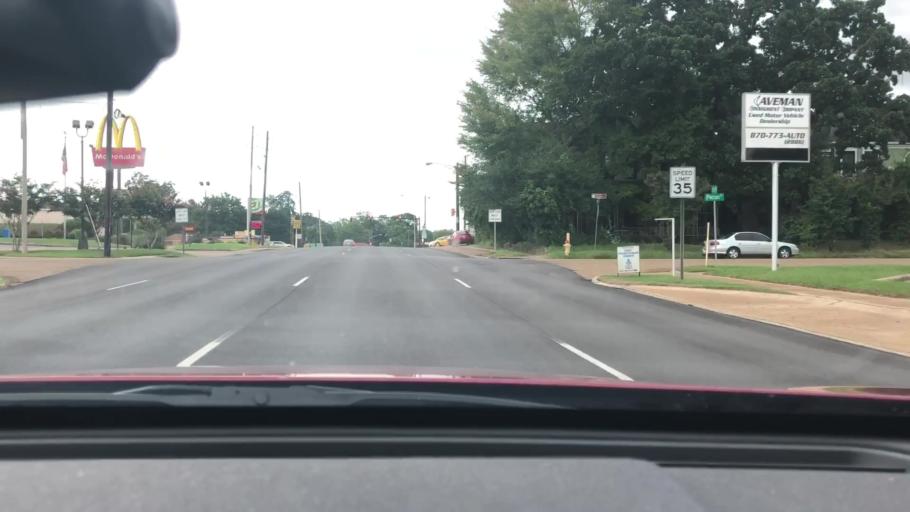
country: US
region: Texas
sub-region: Bowie County
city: Texarkana
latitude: 33.4298
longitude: -94.0375
